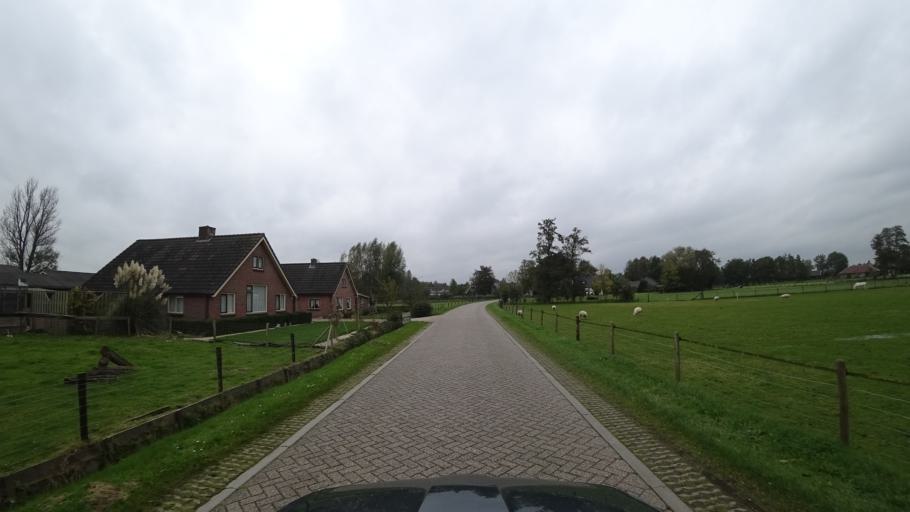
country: NL
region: Gelderland
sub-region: Gemeente Putten
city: Putten
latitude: 52.2542
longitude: 5.5481
